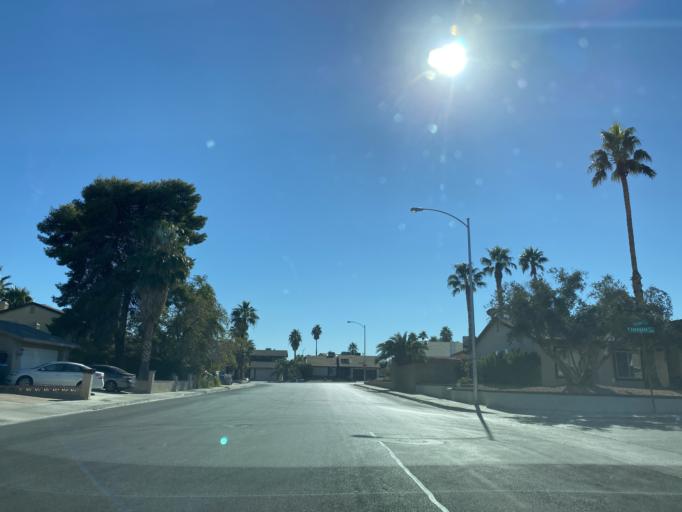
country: US
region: Nevada
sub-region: Clark County
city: Whitney
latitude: 36.0976
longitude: -115.0883
